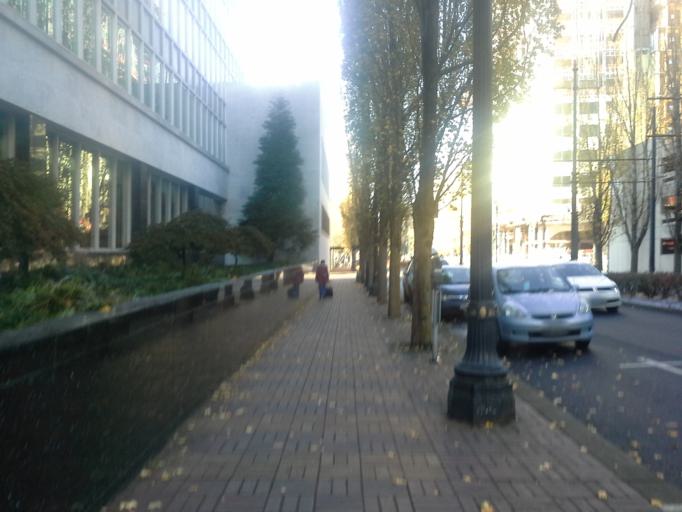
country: US
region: Oregon
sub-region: Multnomah County
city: Portland
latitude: 45.5301
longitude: -122.6555
